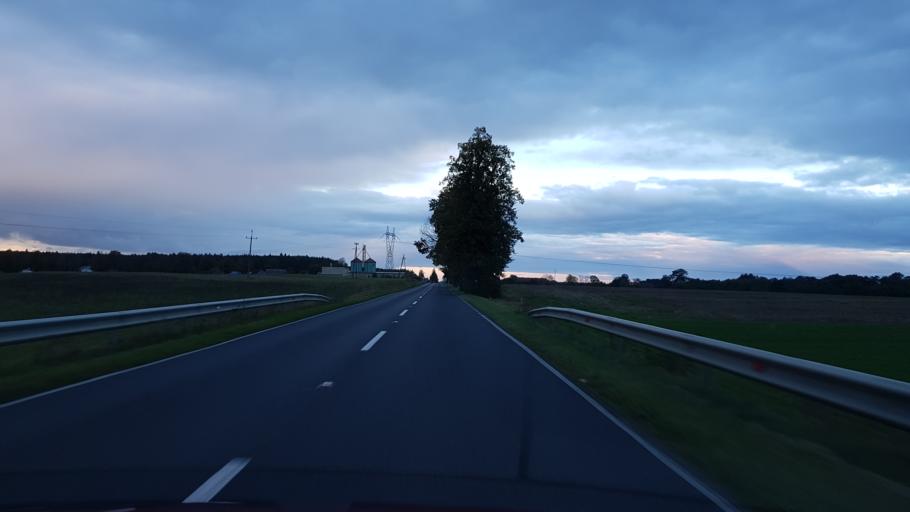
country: PL
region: Greater Poland Voivodeship
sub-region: Powiat zlotowski
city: Krajenka
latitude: 53.2594
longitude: 16.9140
